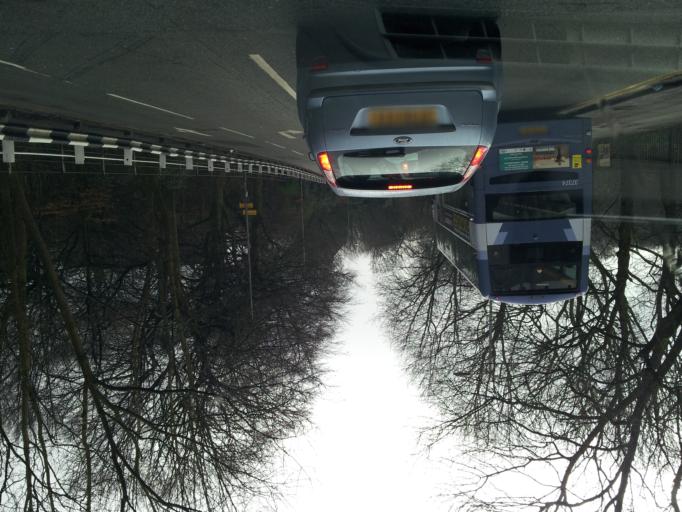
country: GB
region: England
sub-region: Manchester
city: Blackley
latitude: 53.5212
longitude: -2.2146
